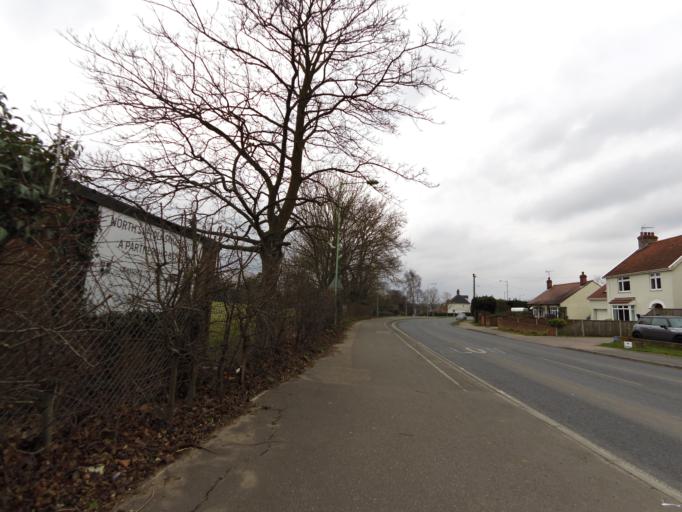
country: GB
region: England
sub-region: Suffolk
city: Halesworth
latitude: 52.3500
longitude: 1.5084
